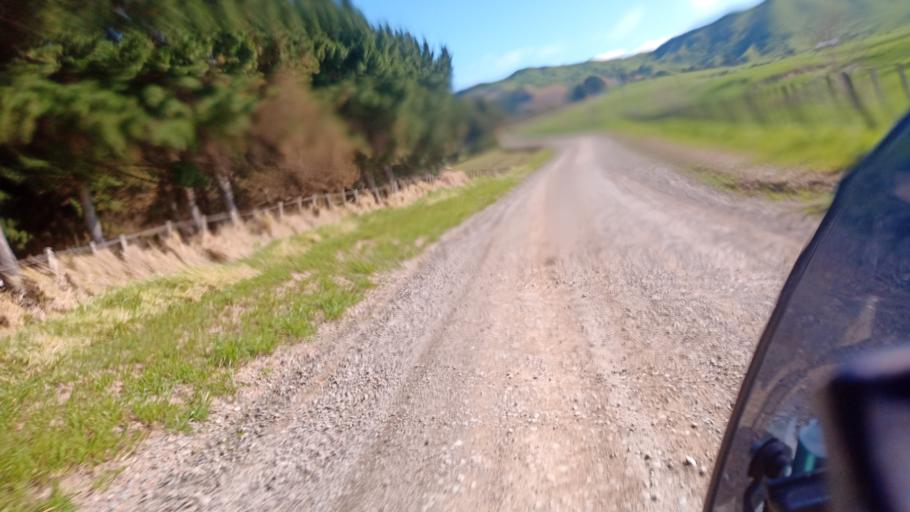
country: NZ
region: Gisborne
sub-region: Gisborne District
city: Gisborne
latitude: -39.1530
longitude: 177.9199
